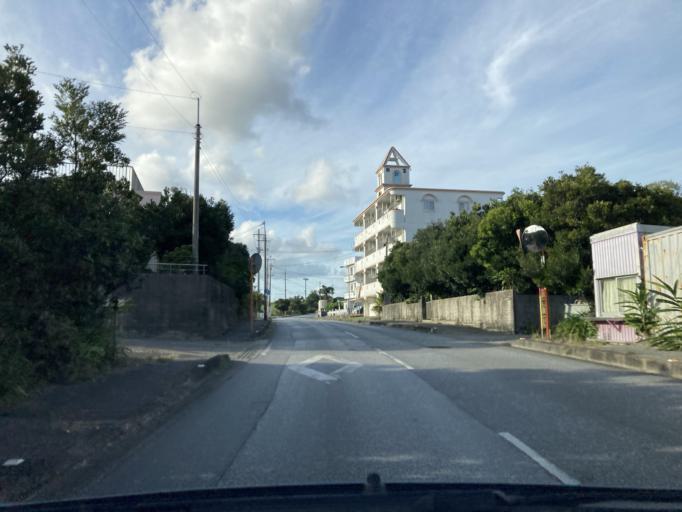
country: JP
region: Okinawa
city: Tomigusuku
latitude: 26.1429
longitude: 127.7474
